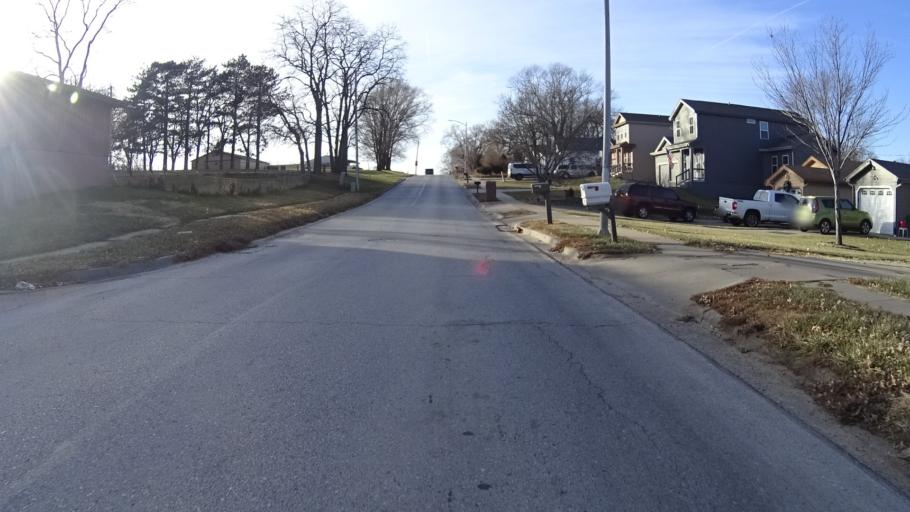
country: US
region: Nebraska
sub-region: Sarpy County
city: La Vista
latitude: 41.1909
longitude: -95.9635
